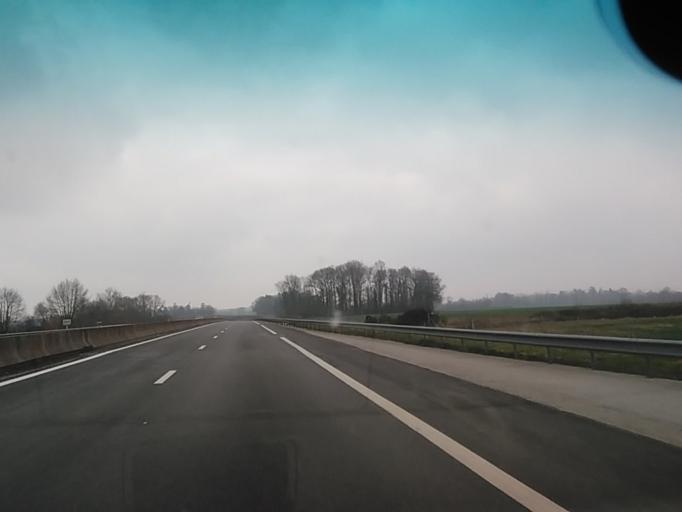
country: FR
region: Lower Normandy
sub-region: Departement de l'Orne
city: Gace
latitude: 48.8573
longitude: 0.3778
